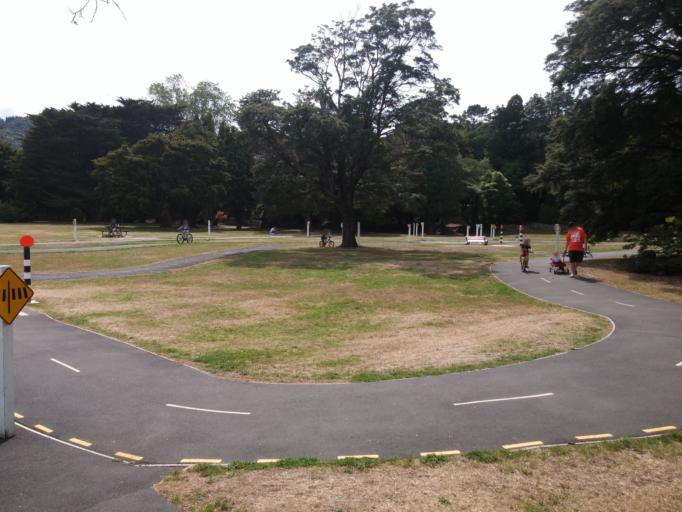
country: NZ
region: Wellington
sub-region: Upper Hutt City
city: Upper Hutt
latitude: -41.1029
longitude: 175.0926
